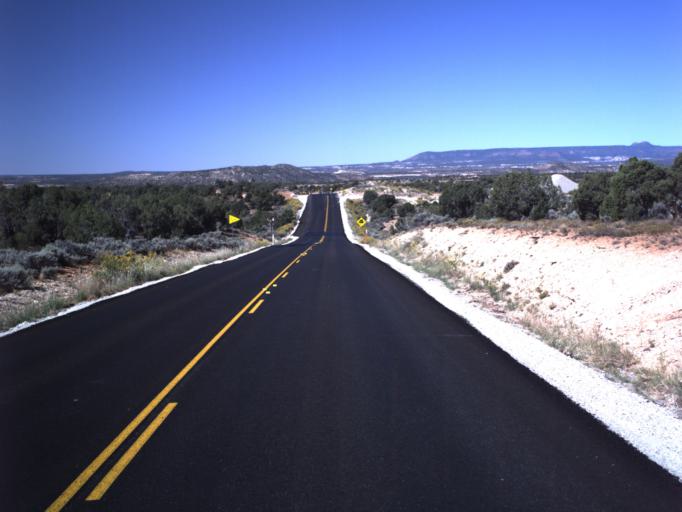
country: US
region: Utah
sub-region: San Juan County
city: Blanding
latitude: 37.5745
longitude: -109.5479
